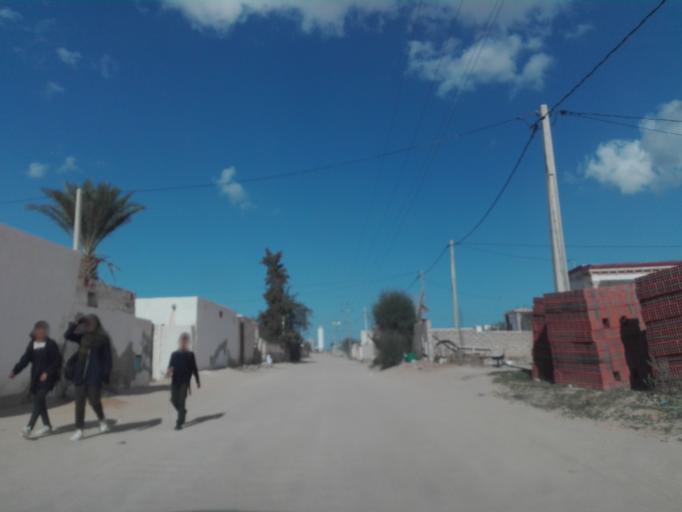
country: TN
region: Madanin
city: Bin Qirdan
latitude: 33.1560
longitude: 11.1939
